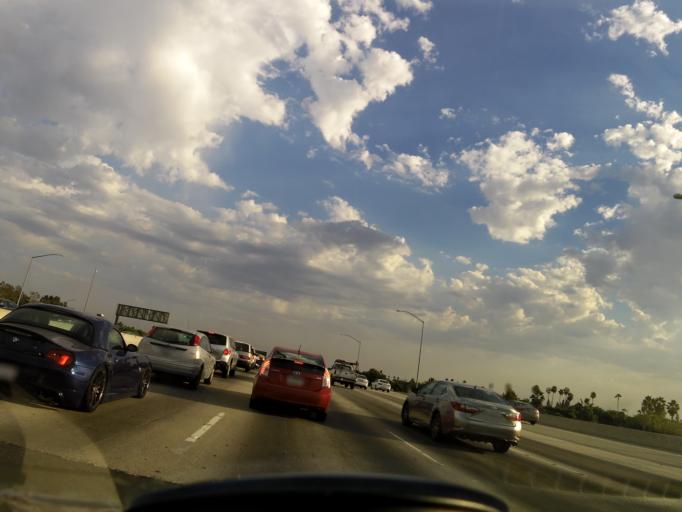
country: US
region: California
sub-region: Orange County
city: Orange
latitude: 33.7882
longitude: -117.8312
